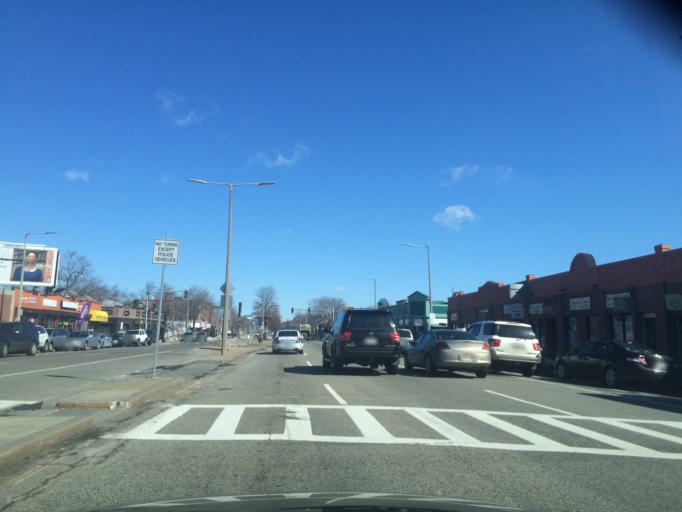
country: US
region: Massachusetts
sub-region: Suffolk County
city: Jamaica Plain
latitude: 42.2847
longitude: -71.0913
